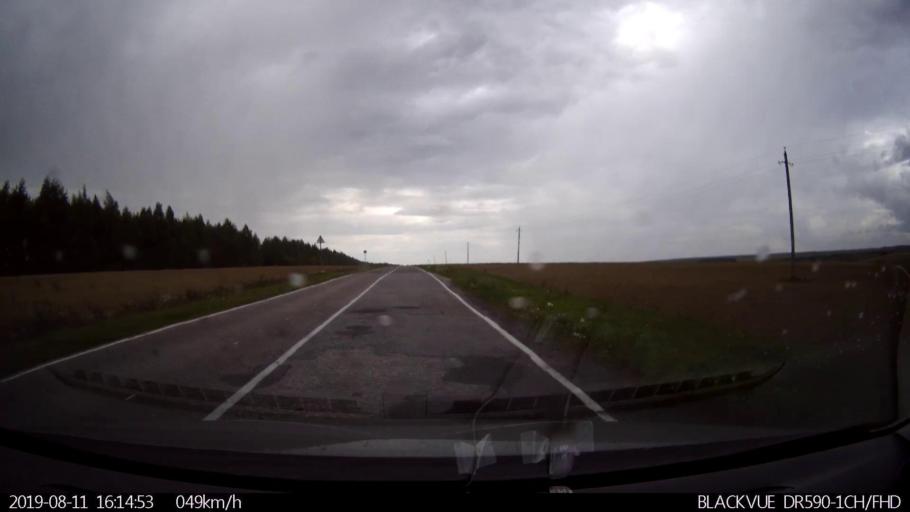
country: RU
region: Ulyanovsk
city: Mayna
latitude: 54.0312
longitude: 47.6315
